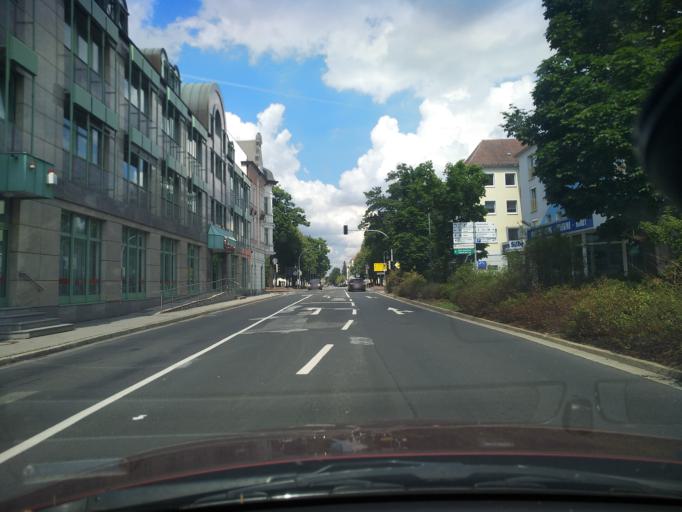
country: DE
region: Saxony
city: Niesky
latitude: 51.2917
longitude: 14.8219
